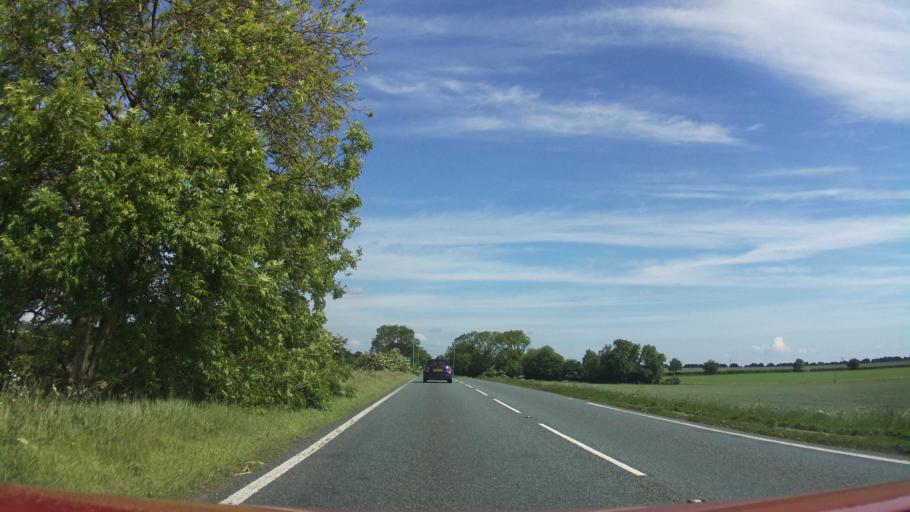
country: GB
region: England
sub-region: Lincolnshire
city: Burton
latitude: 53.2798
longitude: -0.5401
